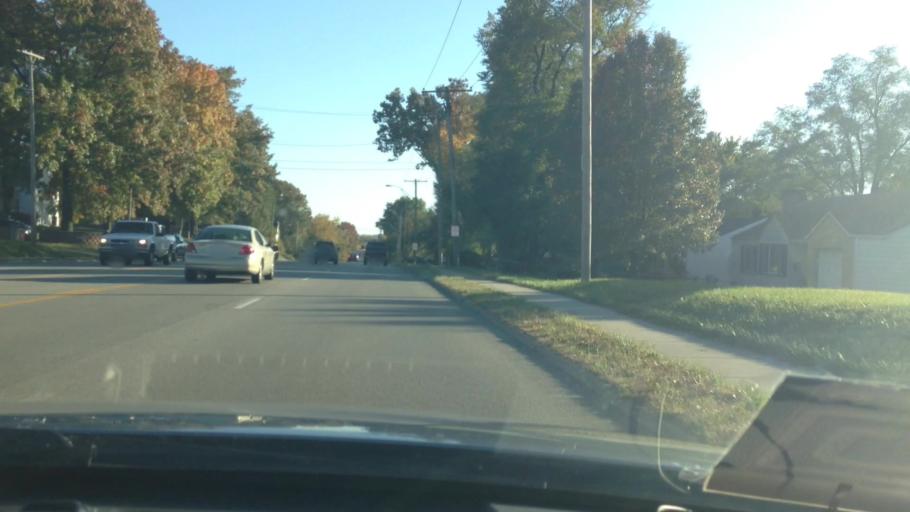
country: US
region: Missouri
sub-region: Clay County
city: Gladstone
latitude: 39.1823
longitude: -94.5490
